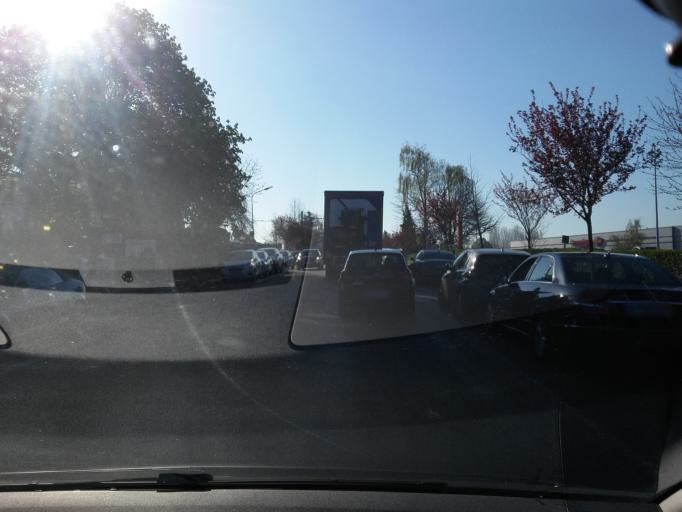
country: BE
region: Wallonia
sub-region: Province du Brabant Wallon
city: Waterloo
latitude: 50.7112
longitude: 4.4017
